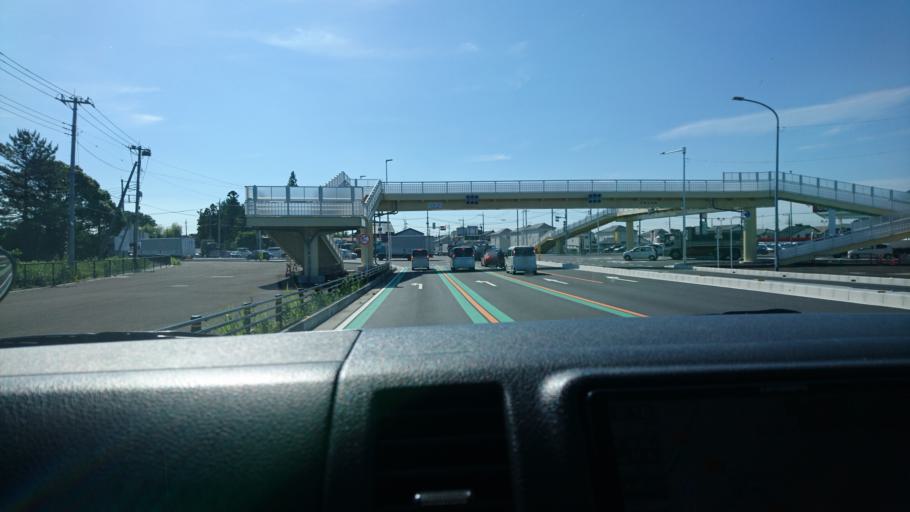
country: JP
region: Saitama
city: Kurihashi
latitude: 36.1205
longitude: 139.6788
